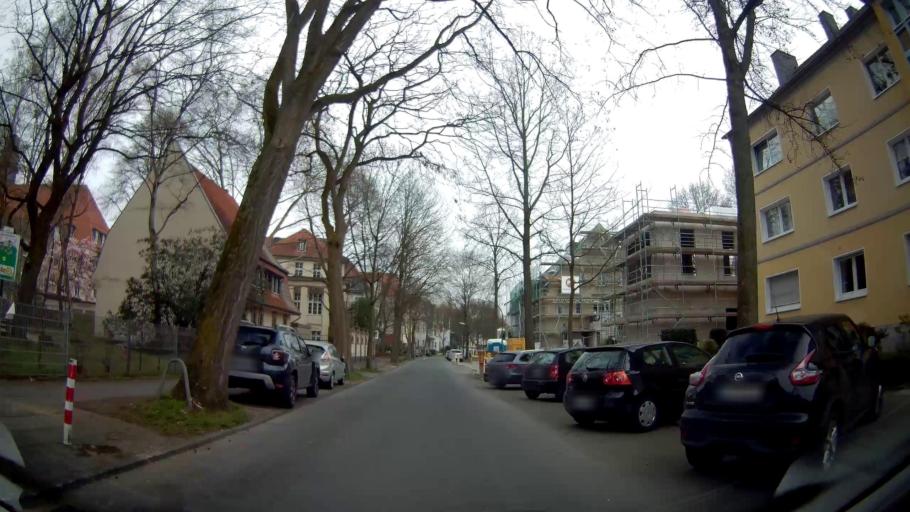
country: DE
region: North Rhine-Westphalia
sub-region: Regierungsbezirk Arnsberg
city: Dortmund
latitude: 51.5106
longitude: 7.4805
